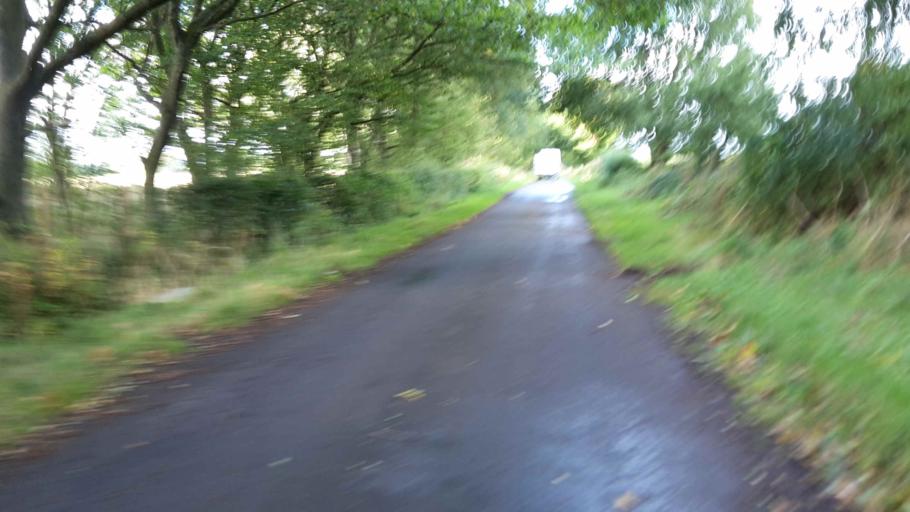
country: GB
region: Scotland
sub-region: South Lanarkshire
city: Carluke
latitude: 55.7247
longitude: -3.8571
